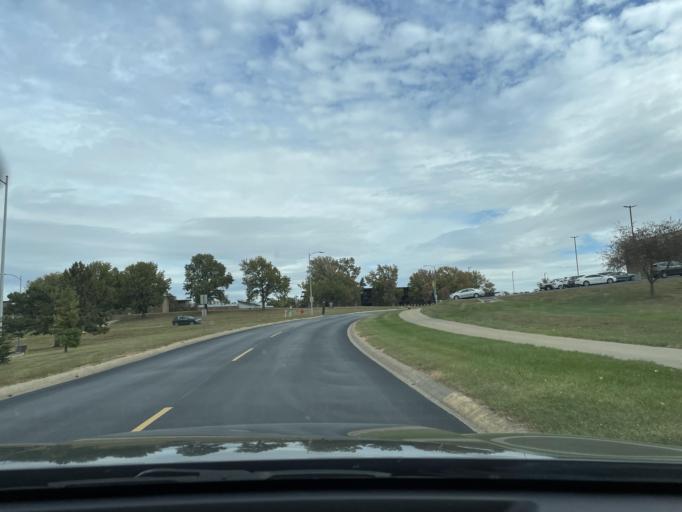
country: US
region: Missouri
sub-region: Buchanan County
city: Saint Joseph
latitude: 39.7590
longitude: -94.7839
